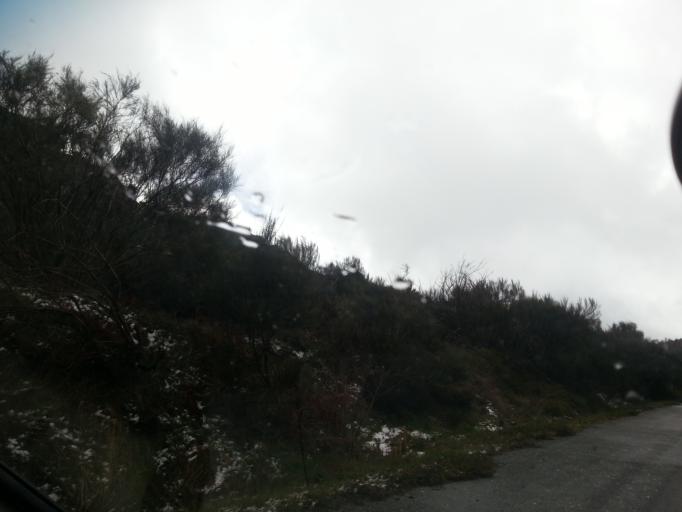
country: PT
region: Guarda
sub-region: Celorico da Beira
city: Celorico da Beira
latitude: 40.5218
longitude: -7.4527
